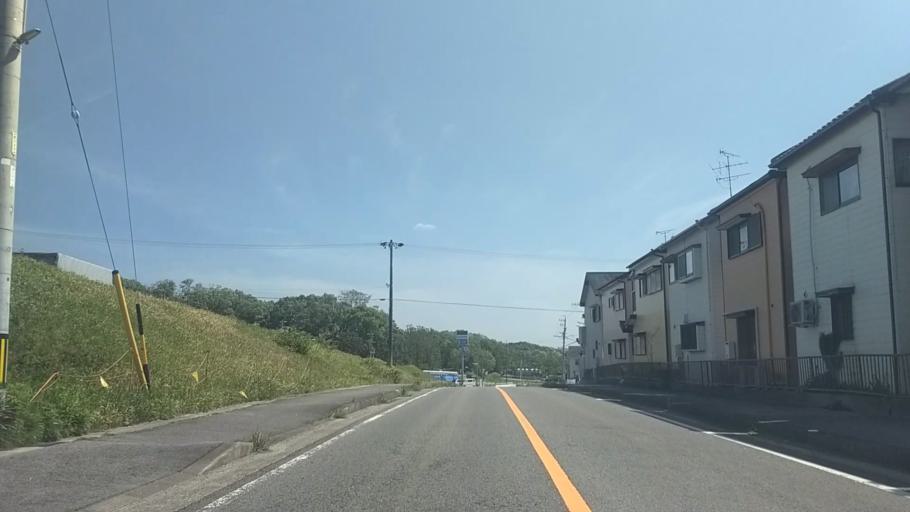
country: JP
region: Aichi
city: Okazaki
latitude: 34.9737
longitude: 137.1858
